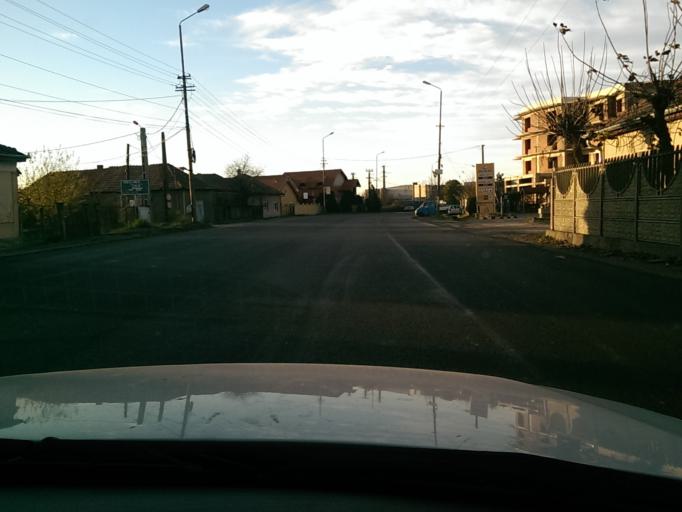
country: RO
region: Bihor
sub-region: Comuna Sanmartin
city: Sanmartin
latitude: 47.0078
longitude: 21.9707
